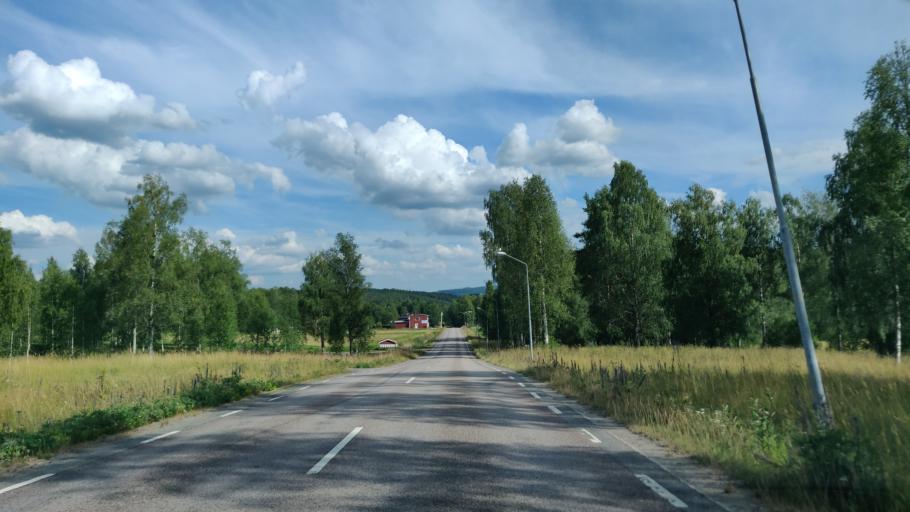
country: SE
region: Vaermland
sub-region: Hagfors Kommun
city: Hagfors
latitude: 60.0662
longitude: 13.6403
